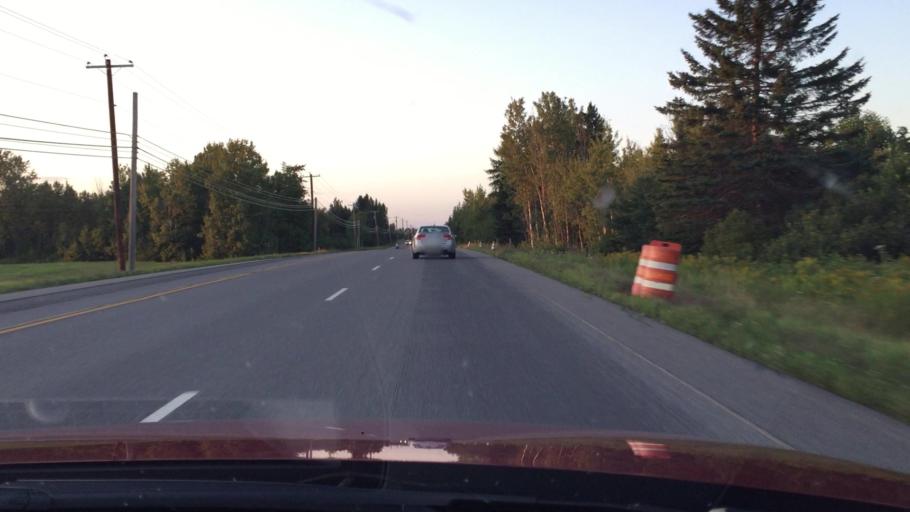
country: US
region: Maine
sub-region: Aroostook County
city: Houlton
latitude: 46.3275
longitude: -67.8416
